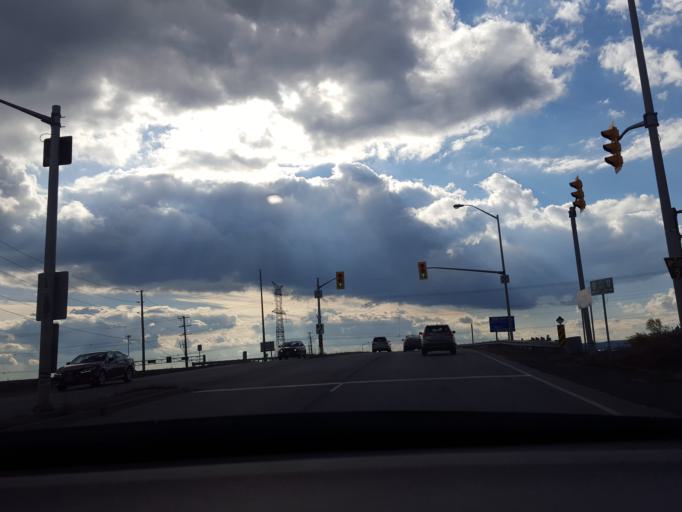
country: CA
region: Ontario
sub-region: Halton
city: Milton
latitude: 43.5729
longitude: -79.7885
